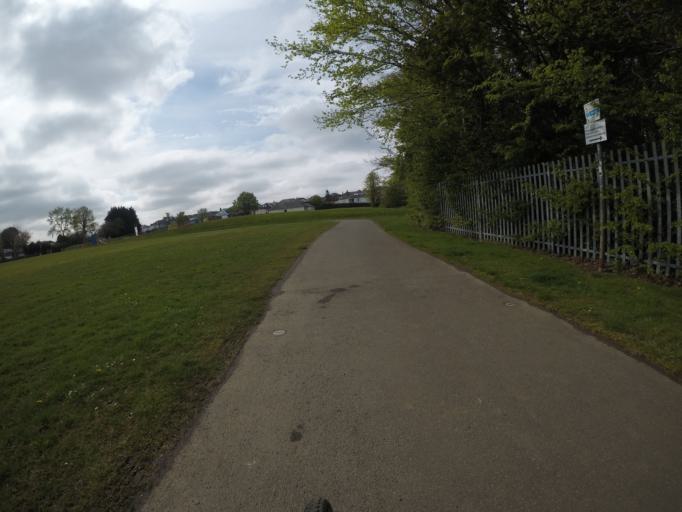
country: GB
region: Scotland
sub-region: East Renfrewshire
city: Giffnock
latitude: 55.8009
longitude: -4.2837
